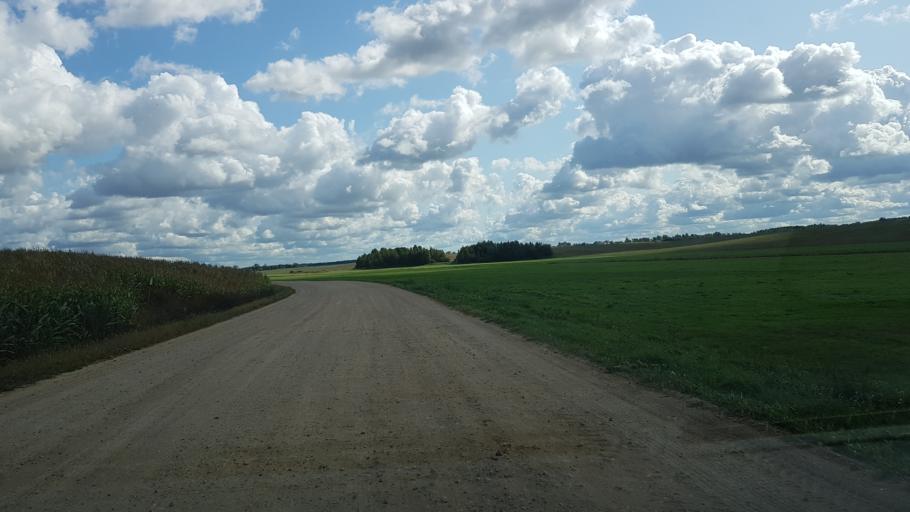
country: BY
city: Fanipol
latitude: 53.7357
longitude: 27.2433
